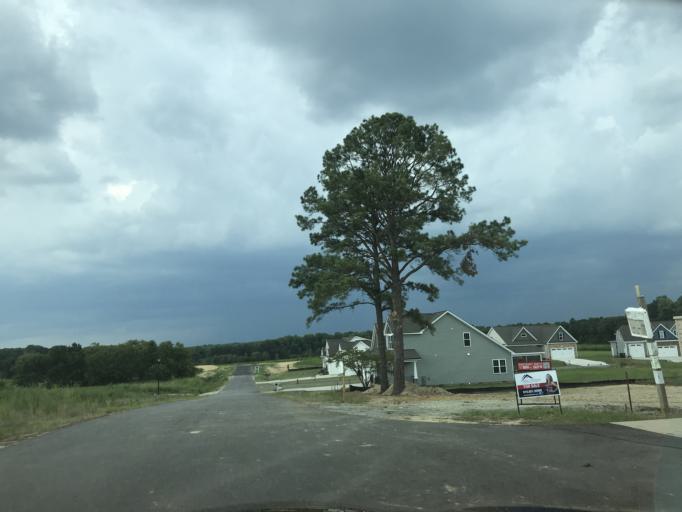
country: US
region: North Carolina
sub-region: Johnston County
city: Four Oaks
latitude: 35.5175
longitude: -78.5315
